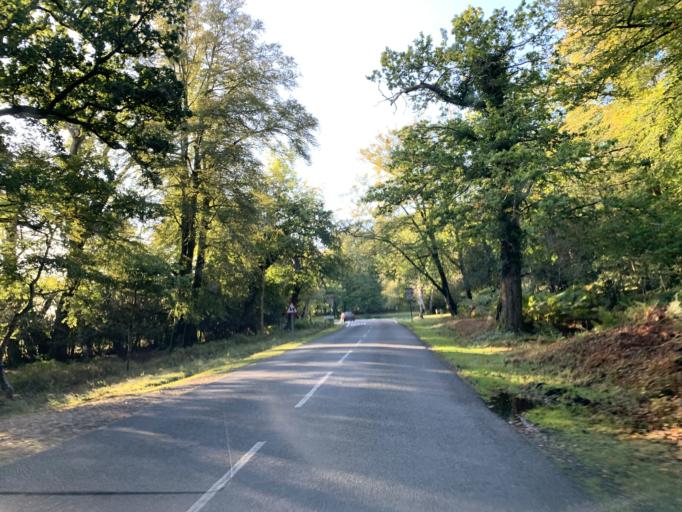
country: GB
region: England
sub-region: Hampshire
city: West Wellow
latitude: 50.9498
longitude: -1.6278
